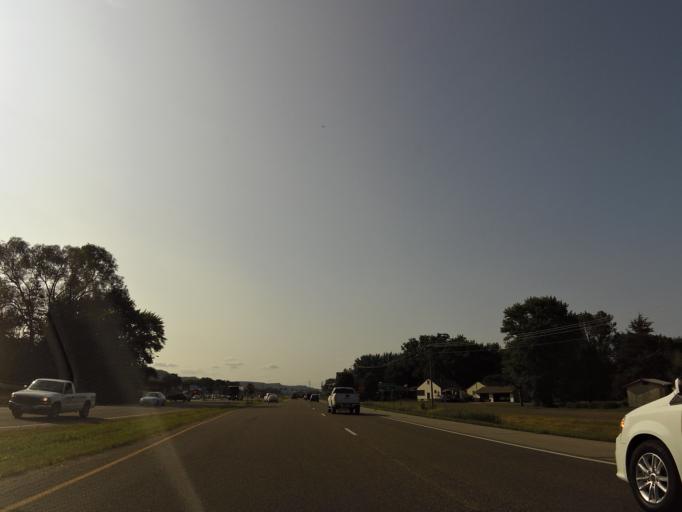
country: US
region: Minnesota
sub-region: Winona County
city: Goodview
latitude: 44.0459
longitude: -91.6725
